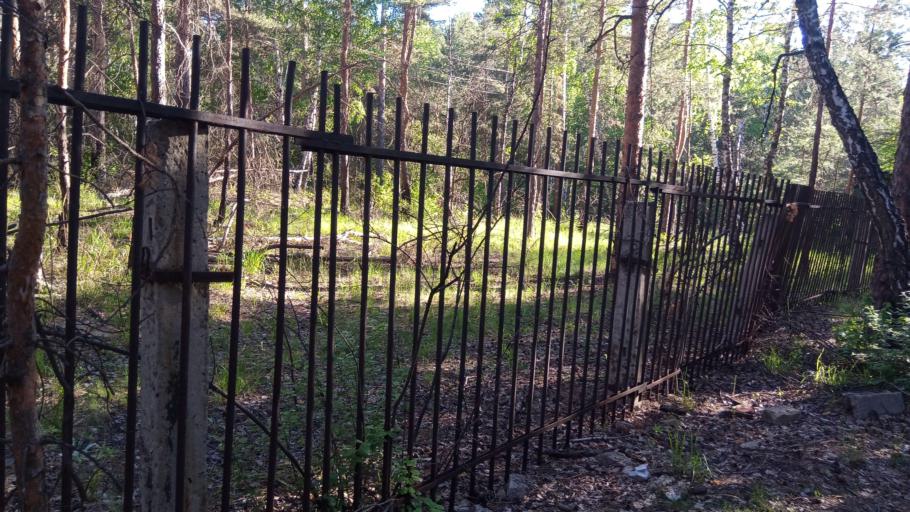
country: RU
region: Chelyabinsk
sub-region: Gorod Chelyabinsk
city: Chelyabinsk
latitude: 55.1300
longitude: 61.3342
